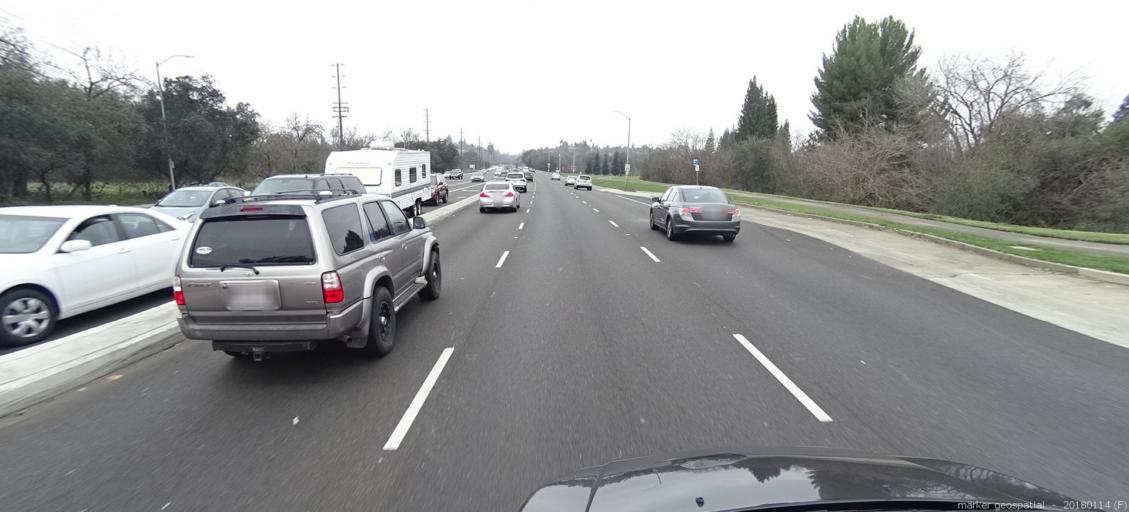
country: US
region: California
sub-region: Sacramento County
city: Fair Oaks
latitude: 38.6281
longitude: -121.2660
